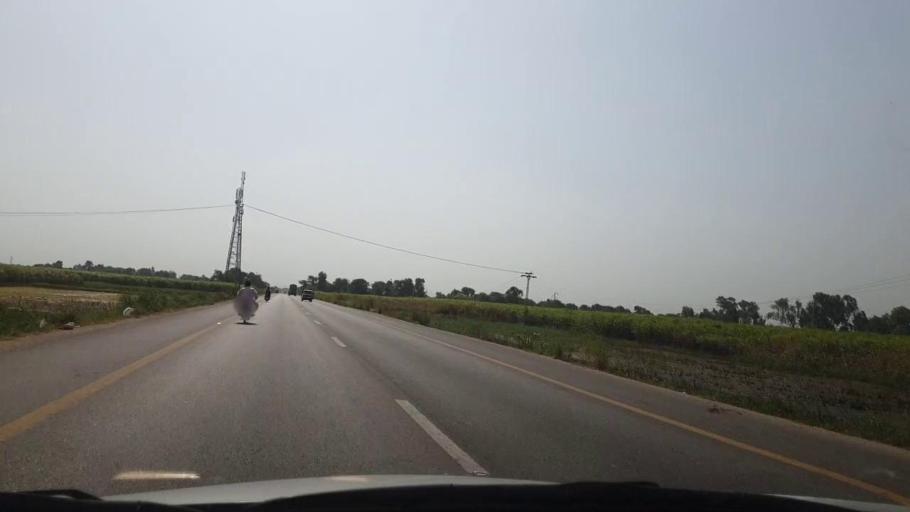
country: PK
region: Sindh
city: Tando Muhammad Khan
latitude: 25.0919
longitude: 68.5988
